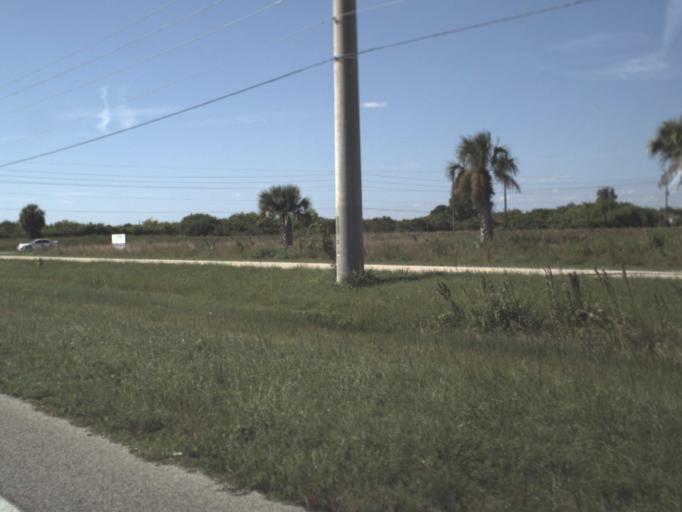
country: US
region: Florida
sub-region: Charlotte County
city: Rotonda
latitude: 26.9328
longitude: -82.2461
